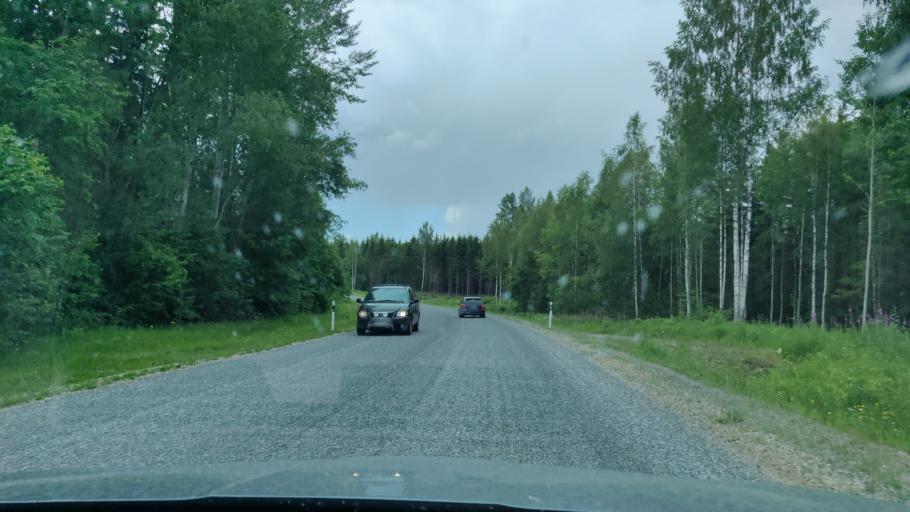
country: EE
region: Vorumaa
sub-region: Antsla vald
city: Vana-Antsla
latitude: 58.0278
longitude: 26.5768
